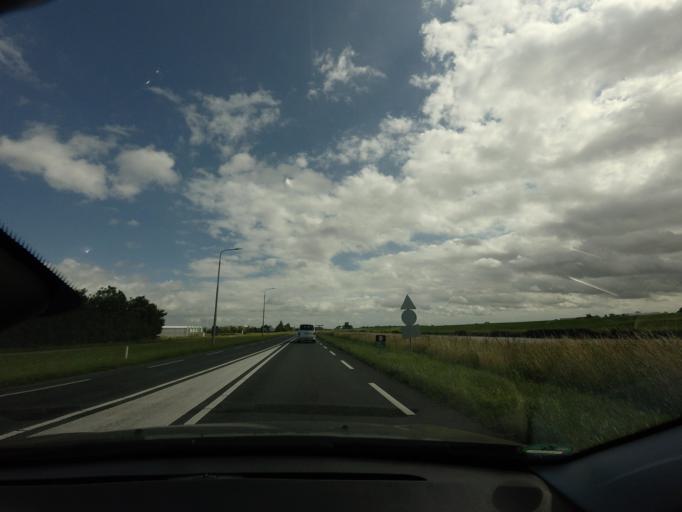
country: NL
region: North Holland
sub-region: Gemeente Den Helder
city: Den Helder
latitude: 52.8965
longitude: 4.7826
